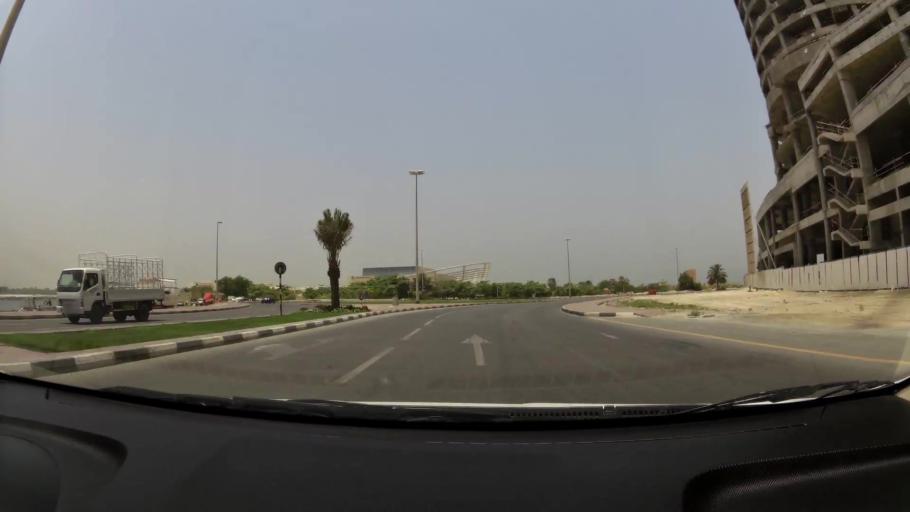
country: AE
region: Ash Shariqah
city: Sharjah
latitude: 25.3311
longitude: 55.3614
